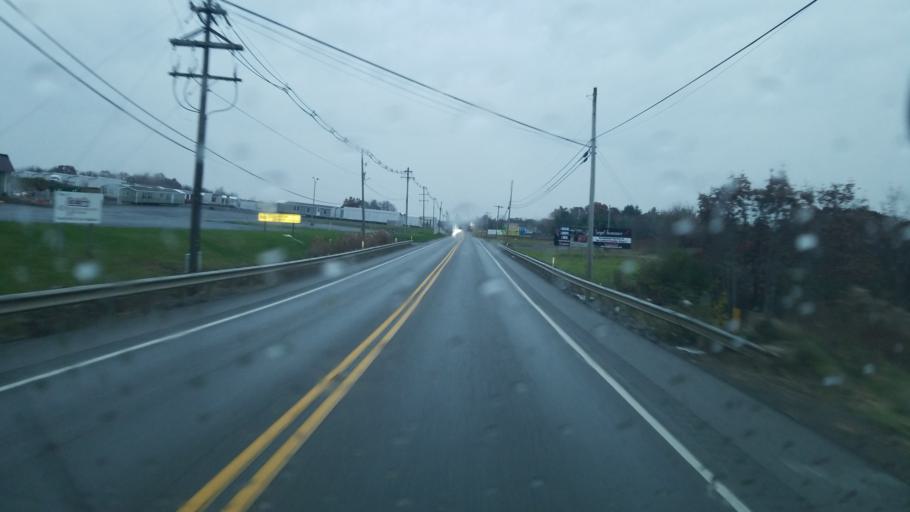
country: US
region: Pennsylvania
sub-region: Clarion County
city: Marianne
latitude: 41.2376
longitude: -79.4288
